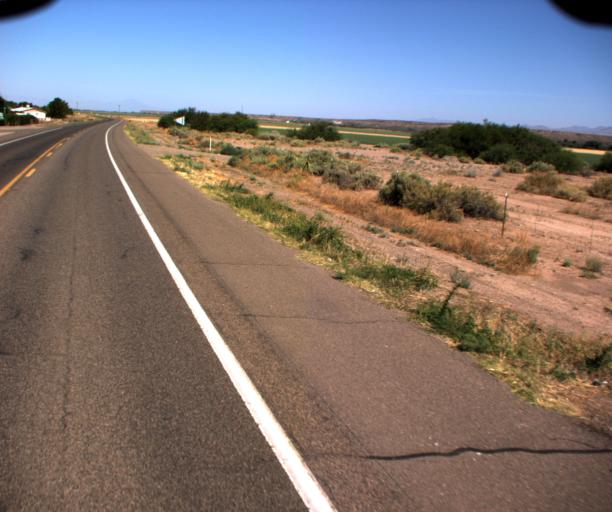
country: US
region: Arizona
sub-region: Graham County
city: Safford
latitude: 32.8139
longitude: -109.6218
